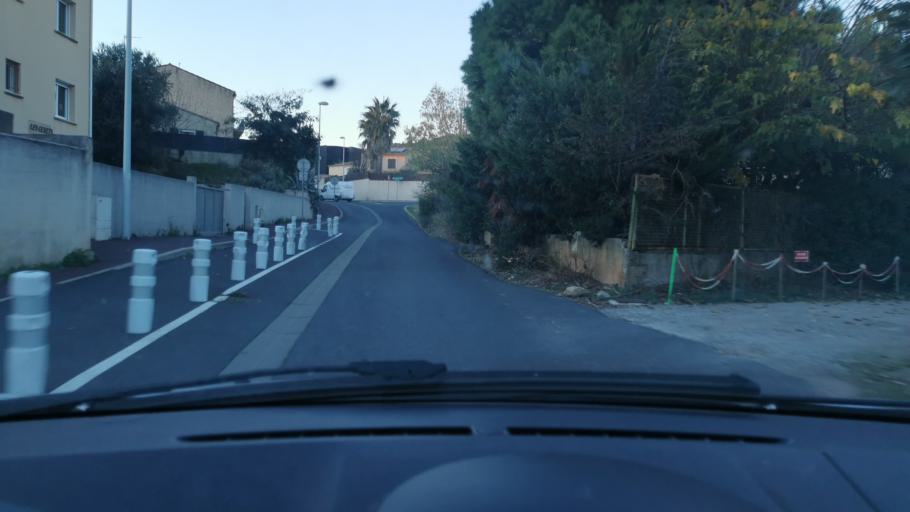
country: FR
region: Languedoc-Roussillon
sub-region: Departement de l'Herault
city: Frontignan
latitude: 43.4546
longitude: 3.7538
